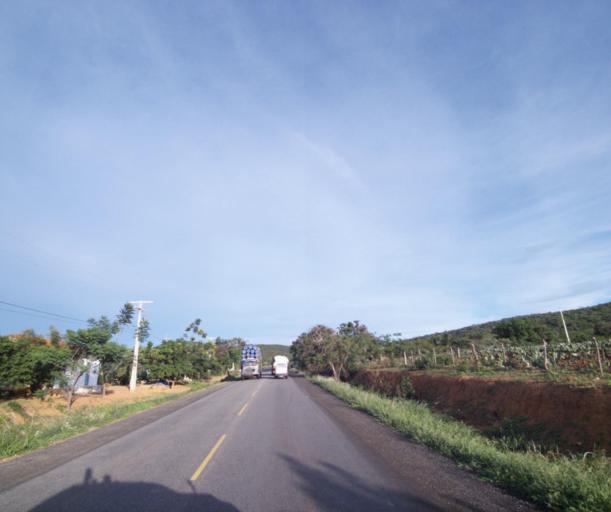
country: BR
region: Bahia
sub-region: Cacule
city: Cacule
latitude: -14.1918
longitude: -42.1524
